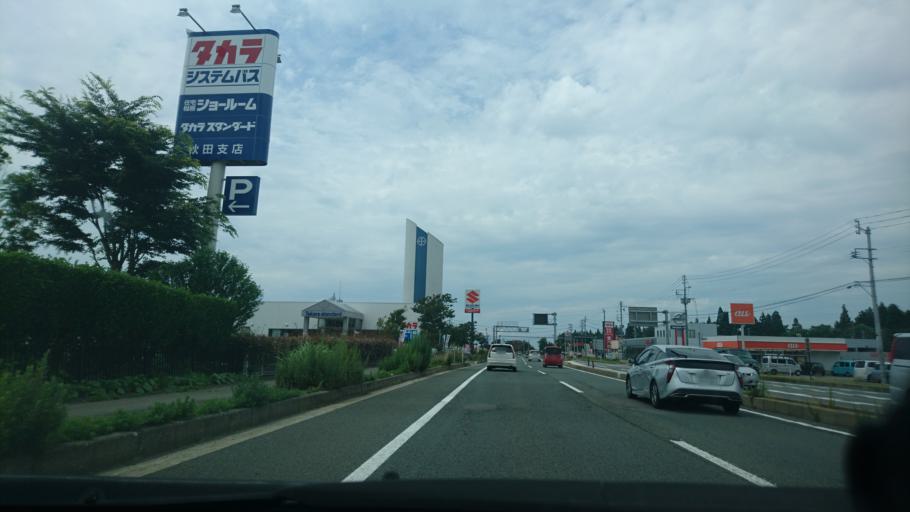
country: JP
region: Akita
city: Akita
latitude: 39.6668
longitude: 140.1673
